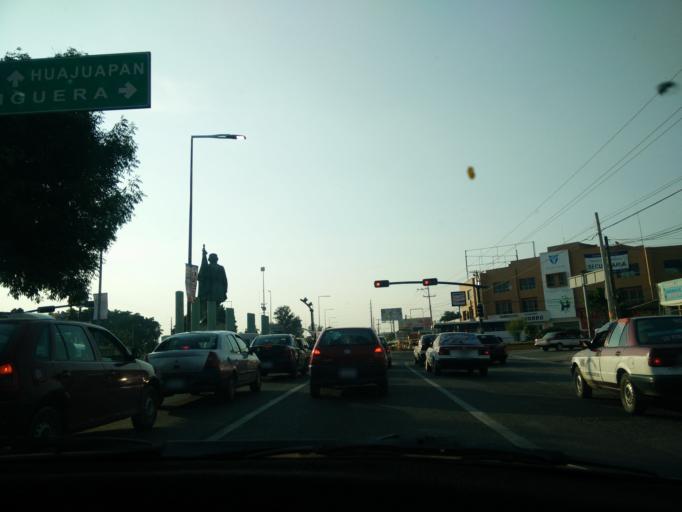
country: MX
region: Oaxaca
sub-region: Santa Maria Atzompa
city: San Jeronimo Yahuiche
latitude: 17.1222
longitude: -96.7639
